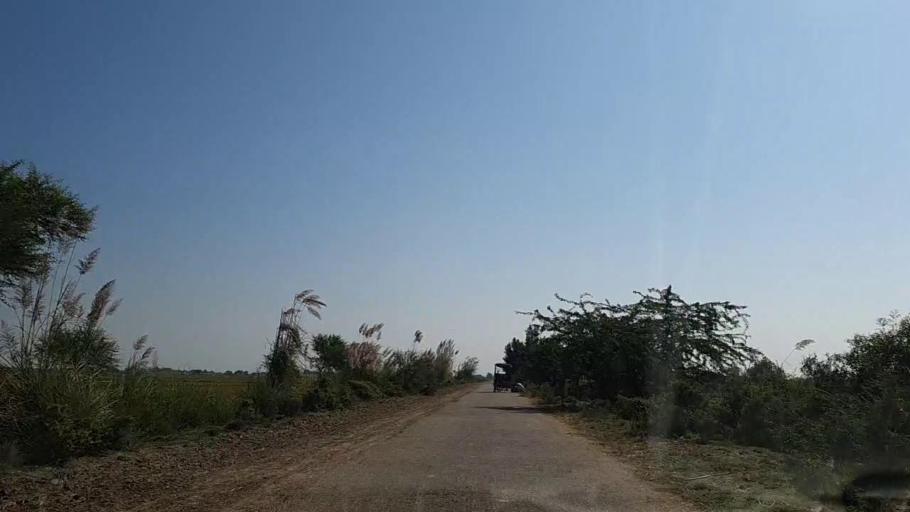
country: PK
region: Sindh
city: Chuhar Jamali
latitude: 24.5250
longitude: 68.0874
